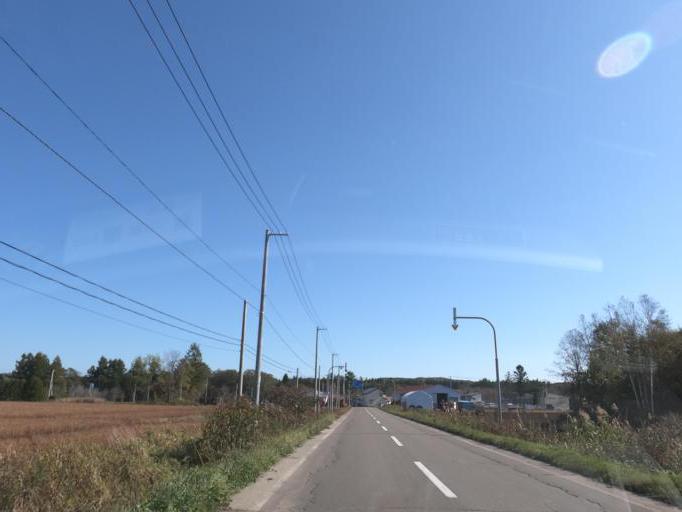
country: JP
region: Hokkaido
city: Obihiro
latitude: 42.6763
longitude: 143.3087
